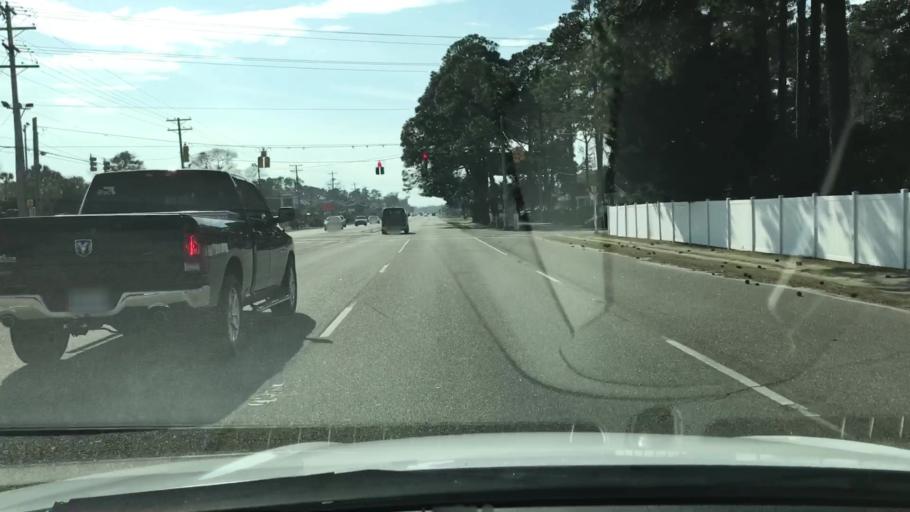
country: US
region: South Carolina
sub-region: Horry County
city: Garden City
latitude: 33.5845
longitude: -79.0146
